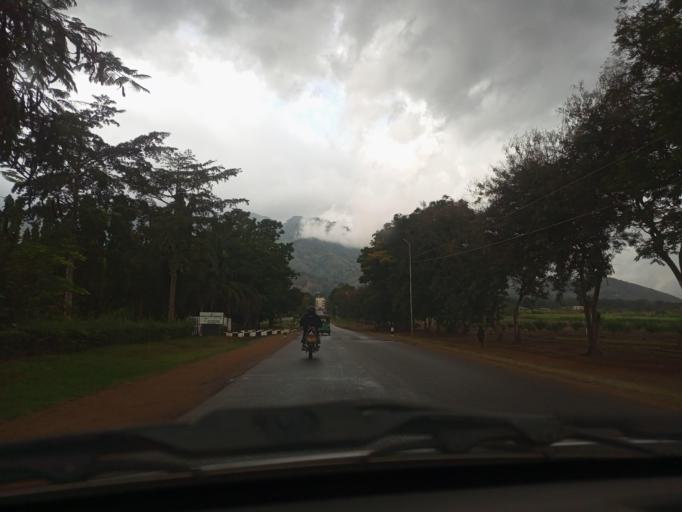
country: TZ
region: Morogoro
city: Morogoro
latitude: -6.8450
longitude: 37.6578
